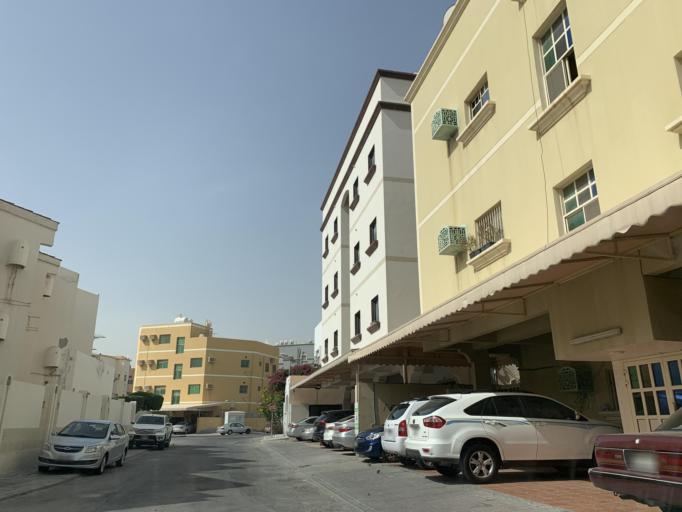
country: BH
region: Northern
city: Madinat `Isa
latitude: 26.1721
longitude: 50.5646
